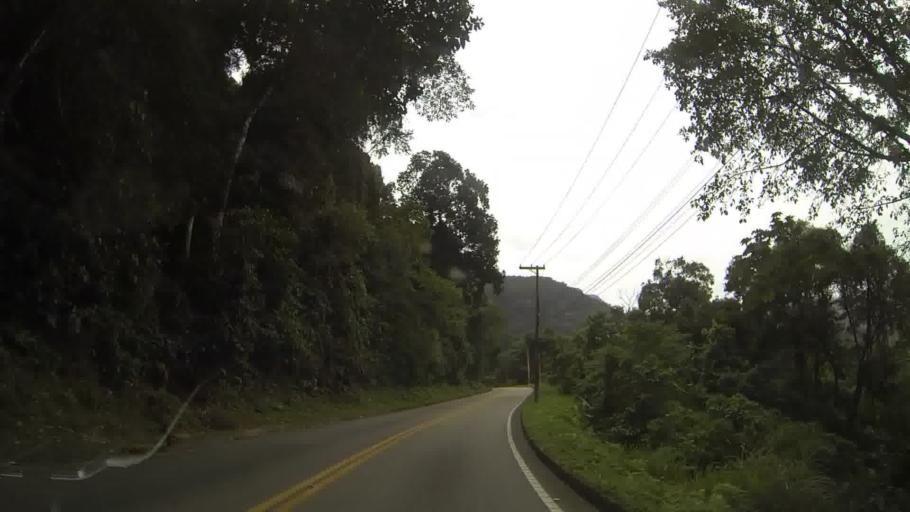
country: BR
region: Sao Paulo
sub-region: Sao Sebastiao
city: Sao Sebastiao
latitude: -23.8156
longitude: -45.4701
